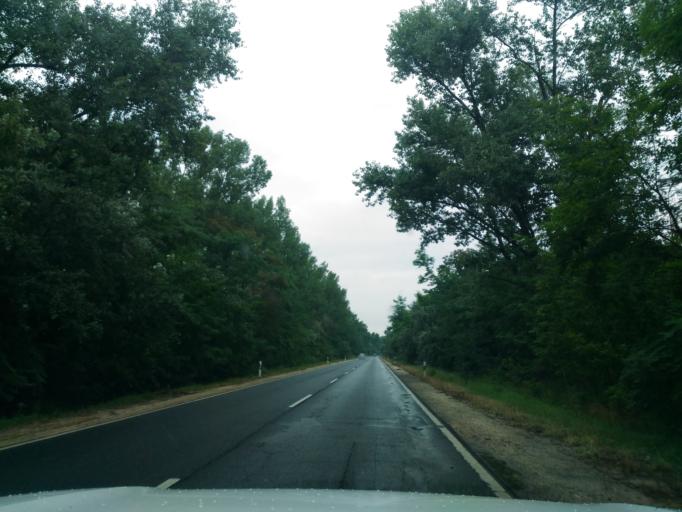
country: HU
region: Pest
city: Ocsa
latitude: 47.2740
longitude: 19.2052
